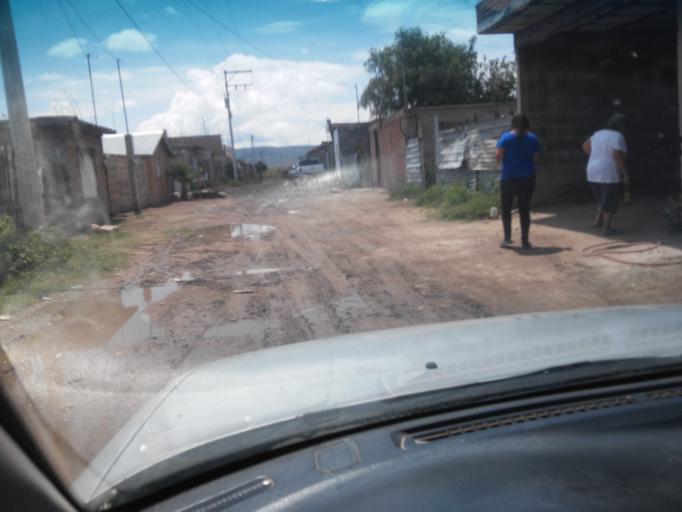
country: MX
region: Durango
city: Victoria de Durango
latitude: 23.9833
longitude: -104.7001
